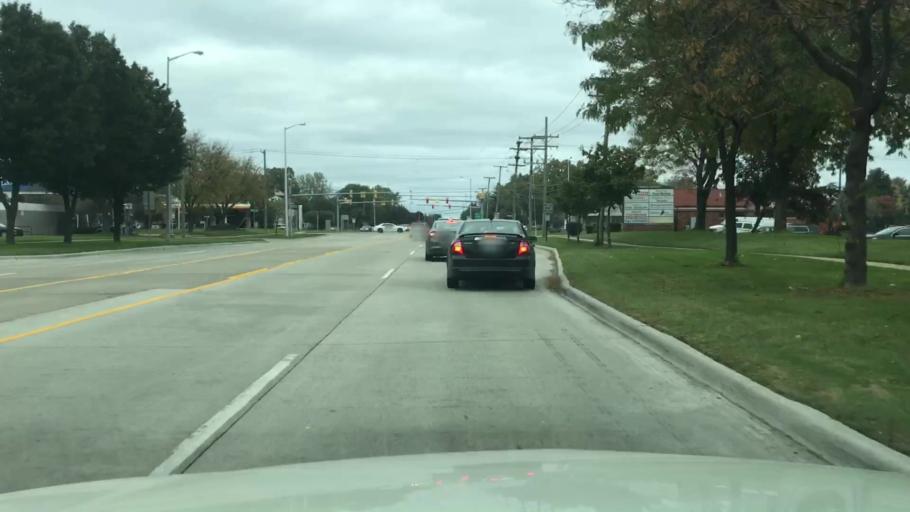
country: US
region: Michigan
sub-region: Macomb County
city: Sterling Heights
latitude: 42.5629
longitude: -83.0697
